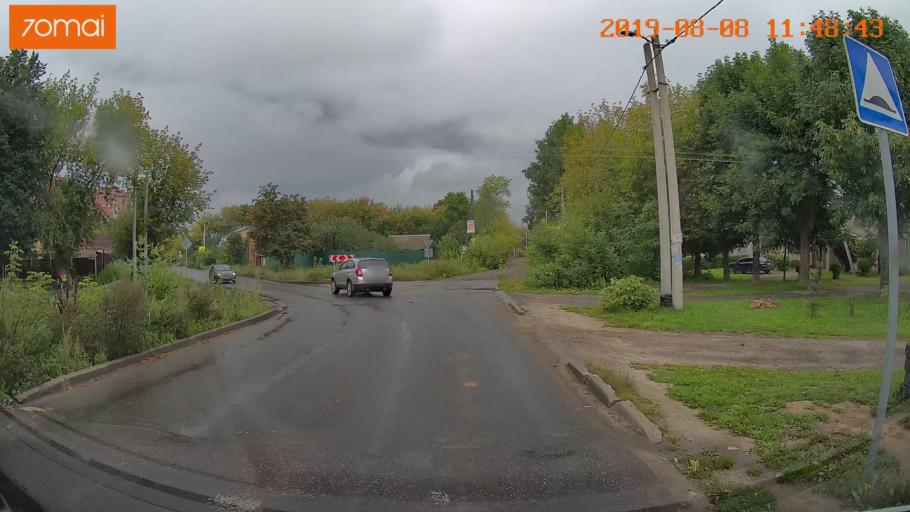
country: RU
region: Ivanovo
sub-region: Gorod Ivanovo
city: Ivanovo
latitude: 56.9753
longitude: 40.9836
